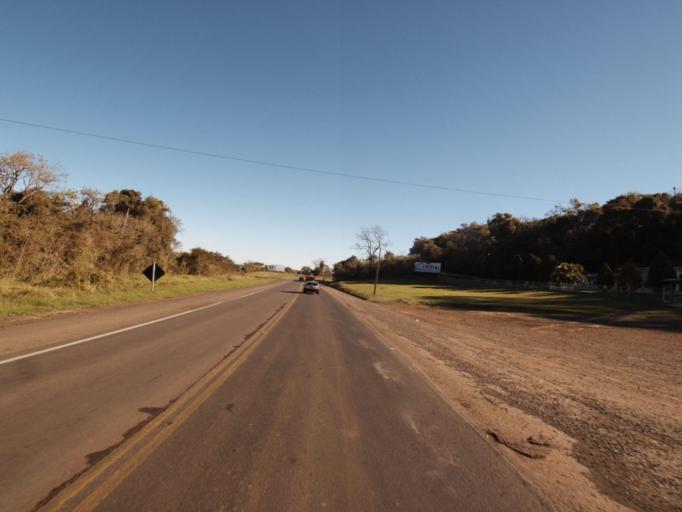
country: BR
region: Santa Catarina
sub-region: Chapeco
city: Chapeco
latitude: -26.9648
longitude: -52.5656
